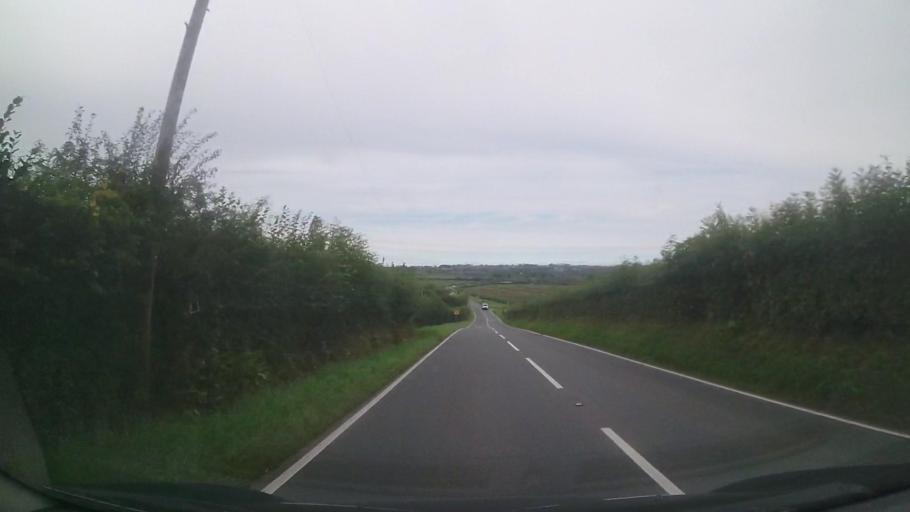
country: GB
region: Wales
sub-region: Pembrokeshire
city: Kilgetty
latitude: 51.7488
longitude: -4.7309
